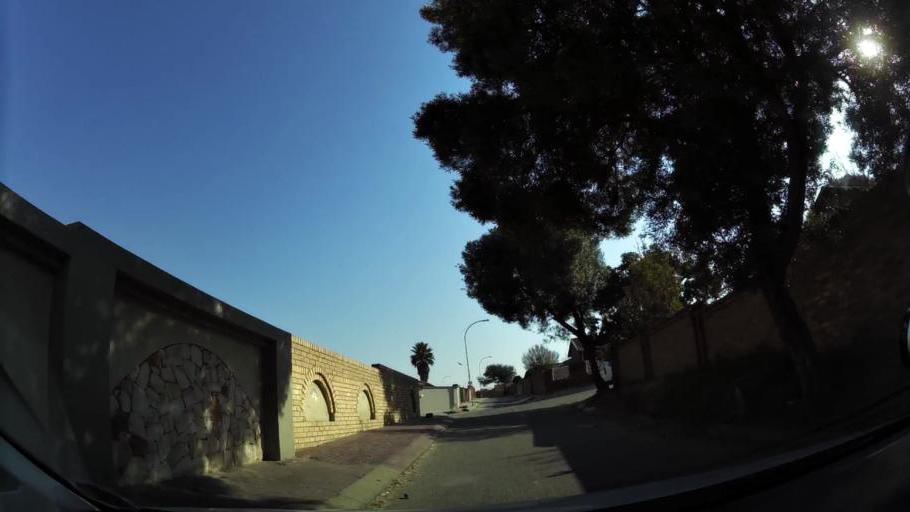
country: ZA
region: Gauteng
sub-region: City of Johannesburg Metropolitan Municipality
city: Modderfontein
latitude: -26.1060
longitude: 28.1125
